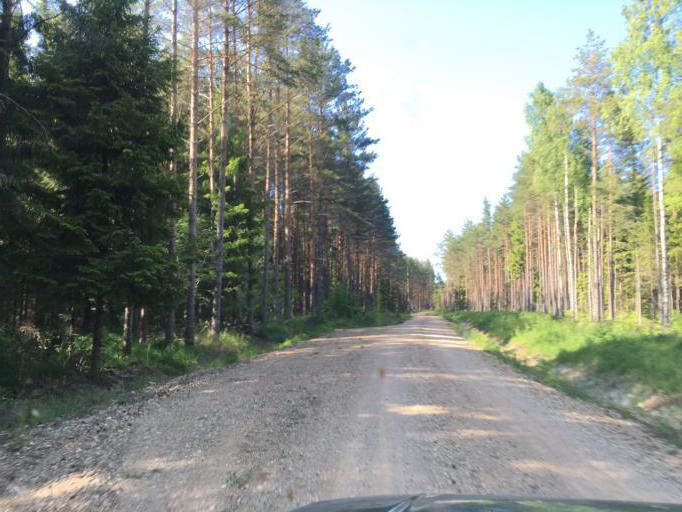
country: LV
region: Dundaga
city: Dundaga
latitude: 57.6077
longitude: 22.5144
